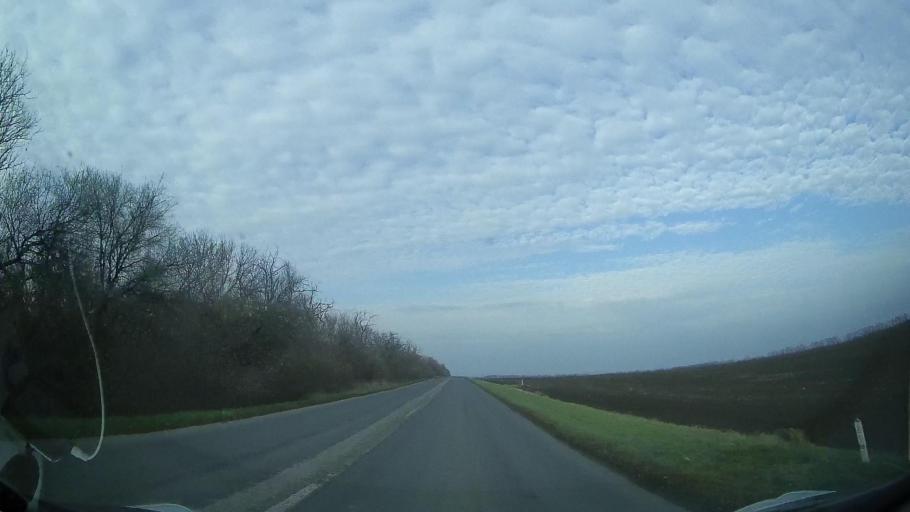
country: RU
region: Rostov
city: Bagayevskaya
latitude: 47.0796
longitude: 40.3915
